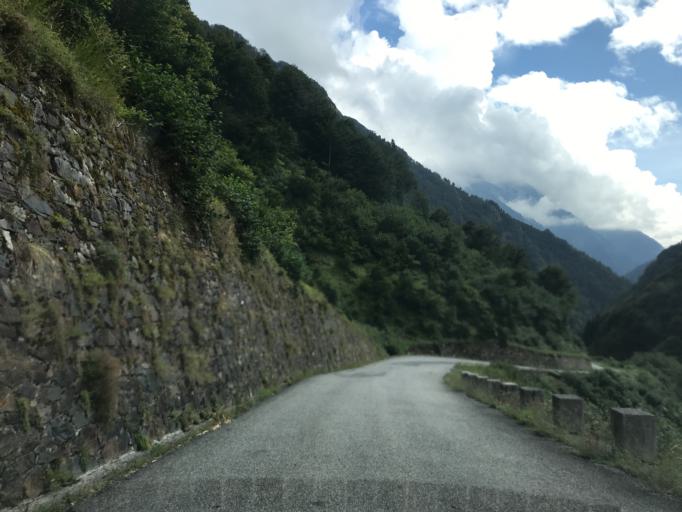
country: FR
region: Midi-Pyrenees
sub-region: Departement des Hautes-Pyrenees
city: Saint-Lary-Soulan
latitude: 42.8085
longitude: 0.2248
